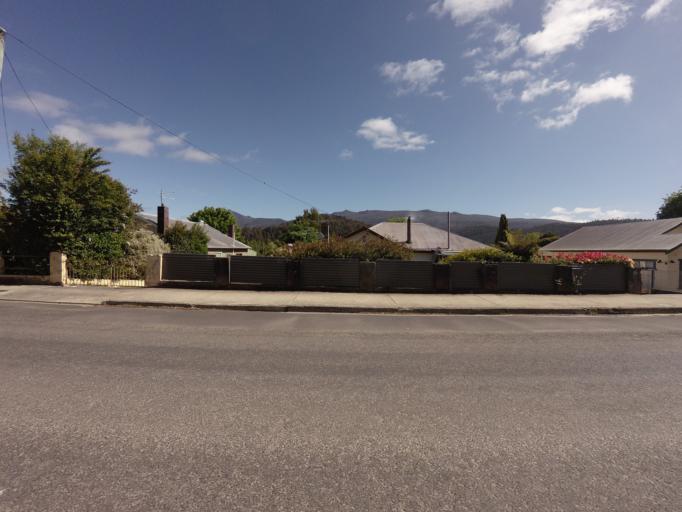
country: AU
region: Tasmania
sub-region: Derwent Valley
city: New Norfolk
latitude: -42.7550
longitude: 146.6274
